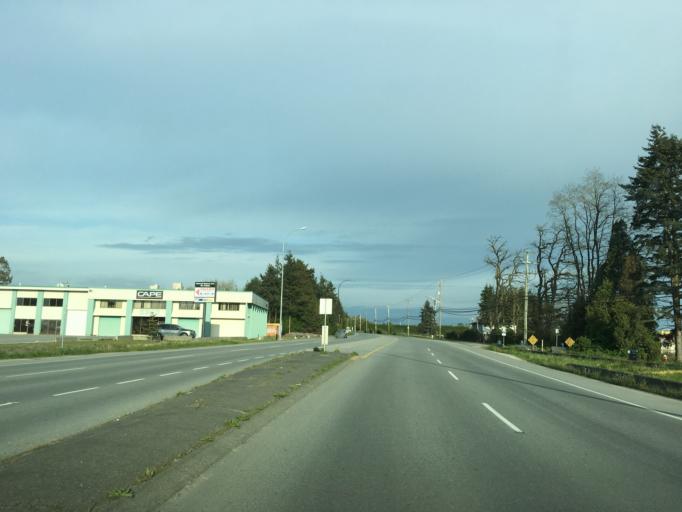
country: CA
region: British Columbia
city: Richmond
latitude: 49.1701
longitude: -123.0682
